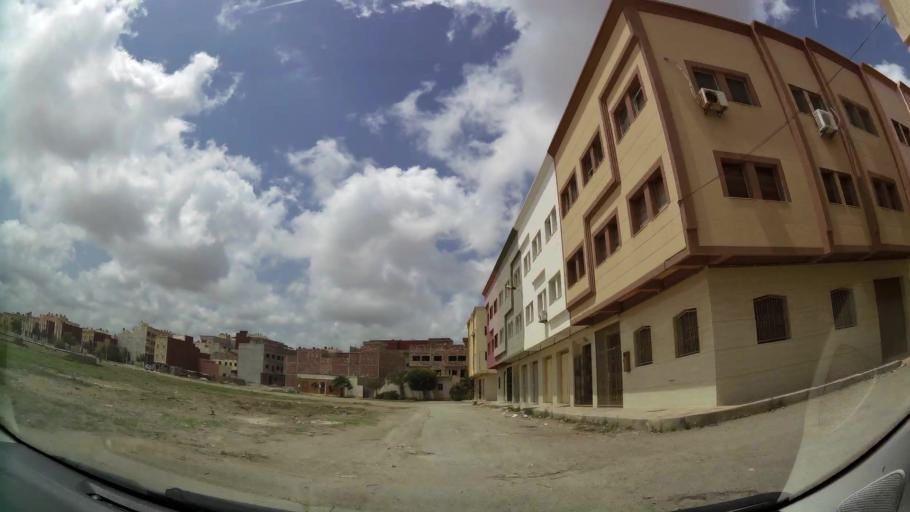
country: MA
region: Oriental
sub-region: Nador
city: Nador
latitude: 35.1651
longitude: -2.9202
